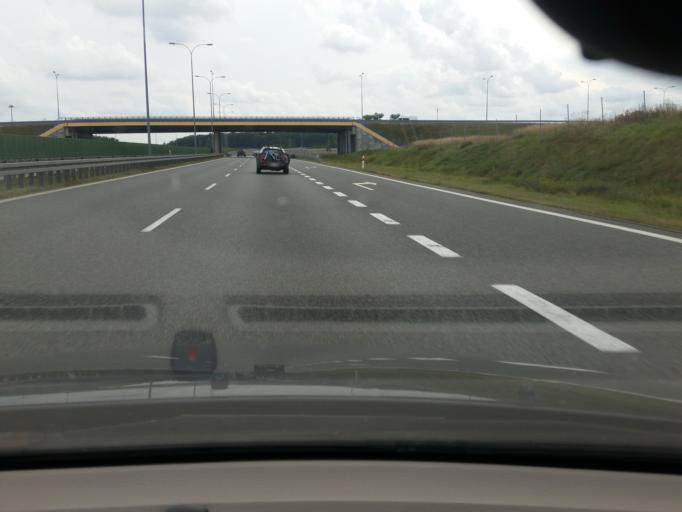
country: PL
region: Pomeranian Voivodeship
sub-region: Powiat tczewski
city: Pelplin
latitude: 53.9340
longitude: 18.6410
